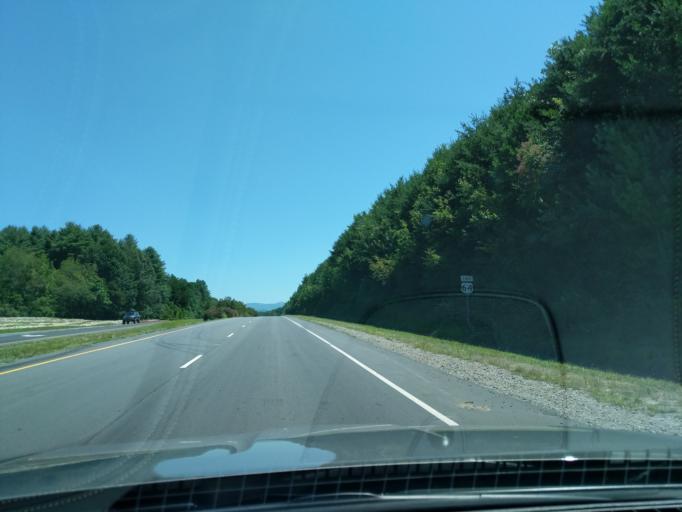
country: US
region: North Carolina
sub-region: Macon County
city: Franklin
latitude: 35.1647
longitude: -83.4238
